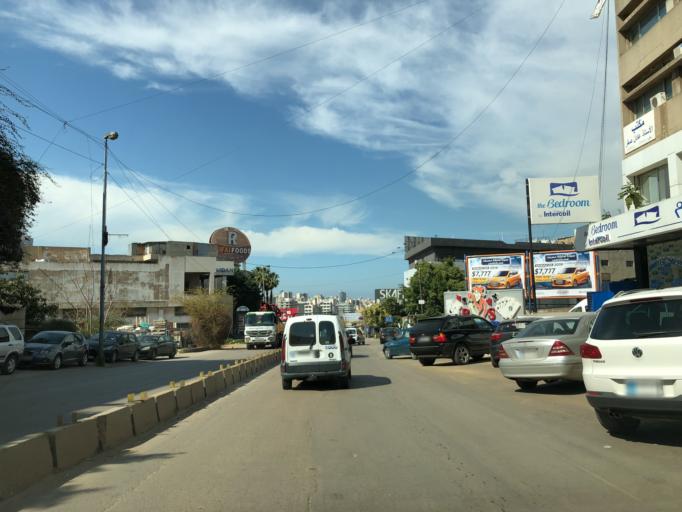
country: LB
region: Mont-Liban
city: Baabda
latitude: 33.8652
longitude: 35.5461
